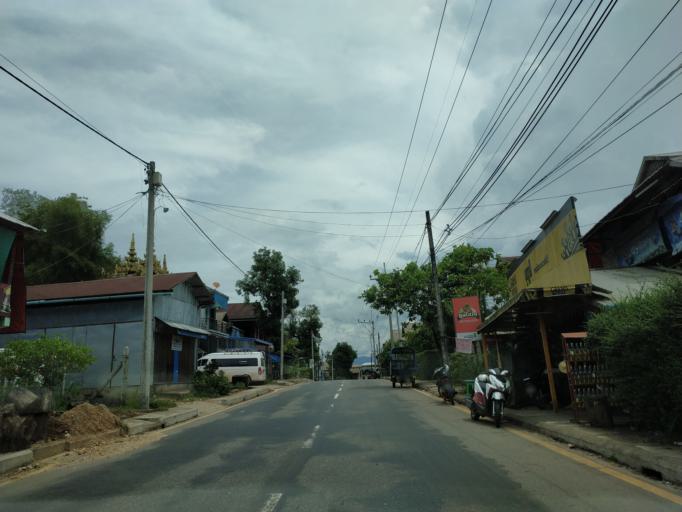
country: MM
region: Tanintharyi
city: Dawei
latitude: 14.0721
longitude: 98.2096
